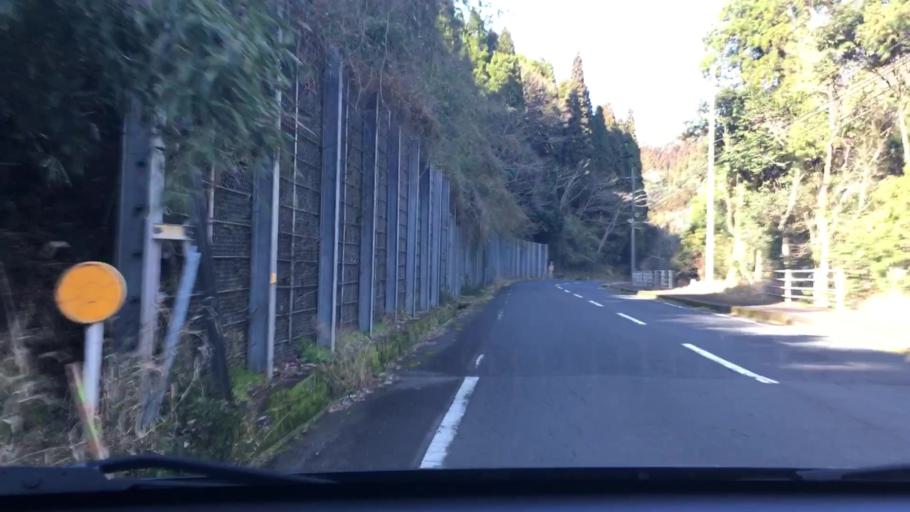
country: JP
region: Kagoshima
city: Satsumasendai
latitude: 31.7531
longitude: 130.4109
